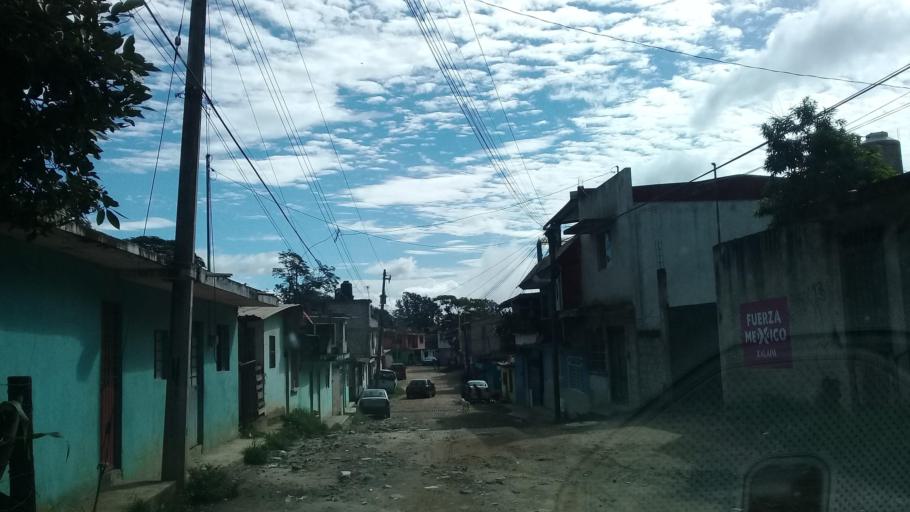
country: MX
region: Veracruz
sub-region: Jilotepec
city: El Pueblito (Garbanzal)
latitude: 19.5739
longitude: -96.9109
